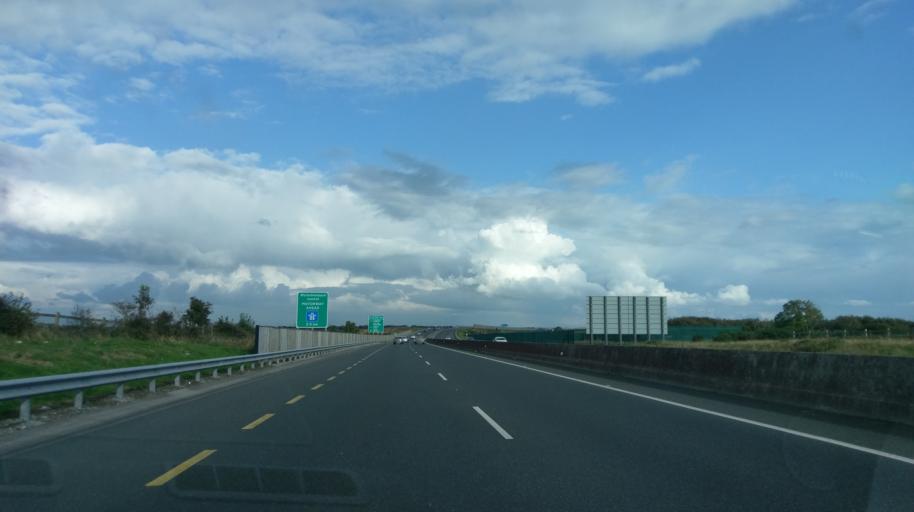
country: IE
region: Connaught
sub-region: County Galway
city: Oranmore
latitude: 53.2907
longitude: -8.9645
